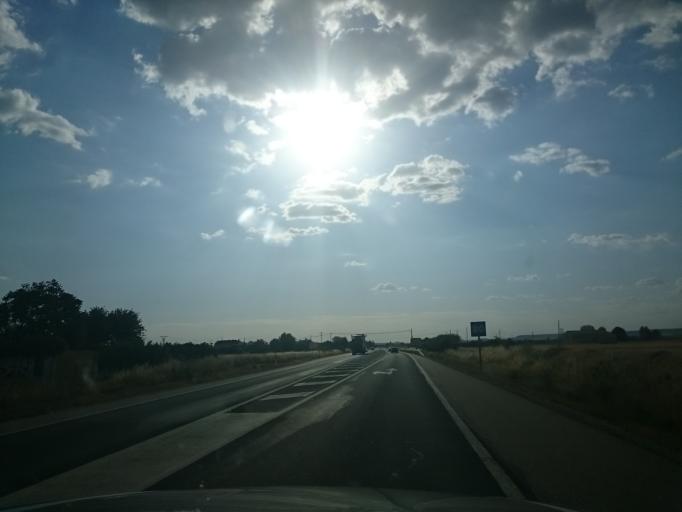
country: ES
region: Castille and Leon
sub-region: Provincia de Burgos
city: Castrillo del Val
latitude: 42.3379
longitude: -3.5920
